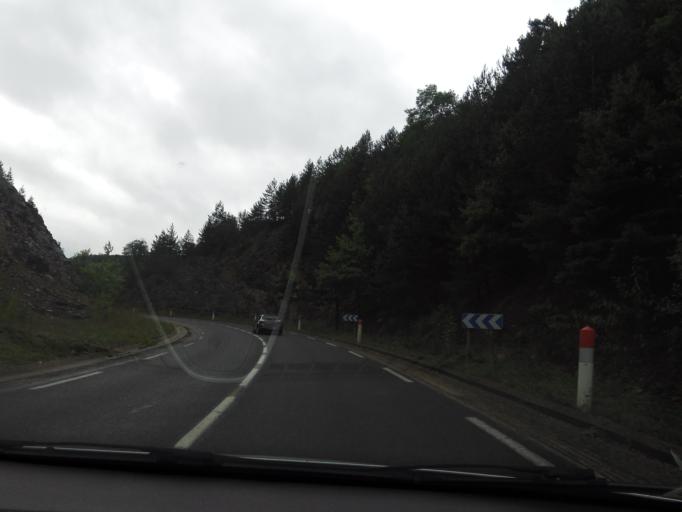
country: FR
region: Languedoc-Roussillon
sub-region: Departement de la Lozere
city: Chirac
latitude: 44.4936
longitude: 3.2622
